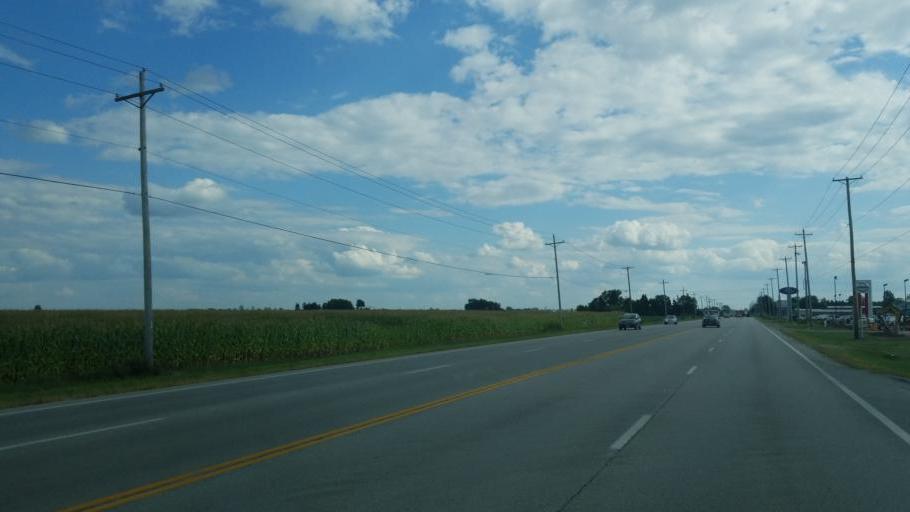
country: US
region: Ohio
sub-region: Wood County
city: Bowling Green
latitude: 41.4176
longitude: -83.6509
